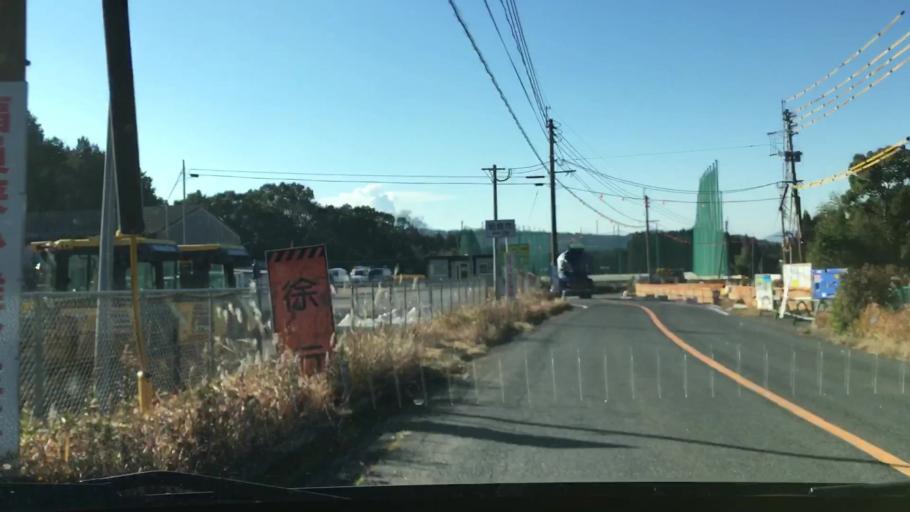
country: JP
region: Kagoshima
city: Kajiki
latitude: 31.7745
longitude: 130.7004
